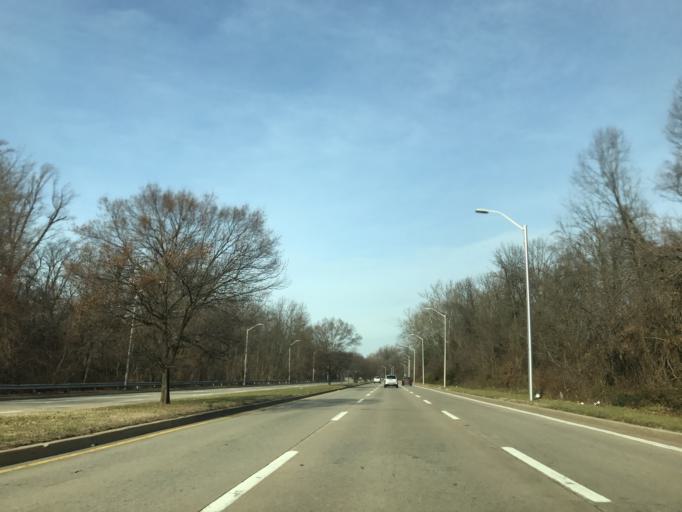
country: US
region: Maryland
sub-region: Baltimore County
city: Parkville
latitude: 39.3620
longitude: -76.5730
